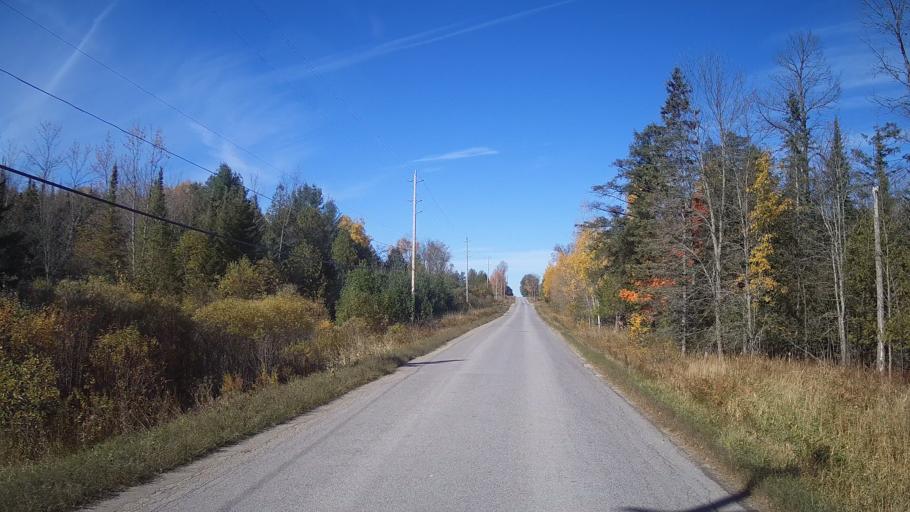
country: CA
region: Ontario
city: Perth
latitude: 44.8497
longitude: -76.3709
